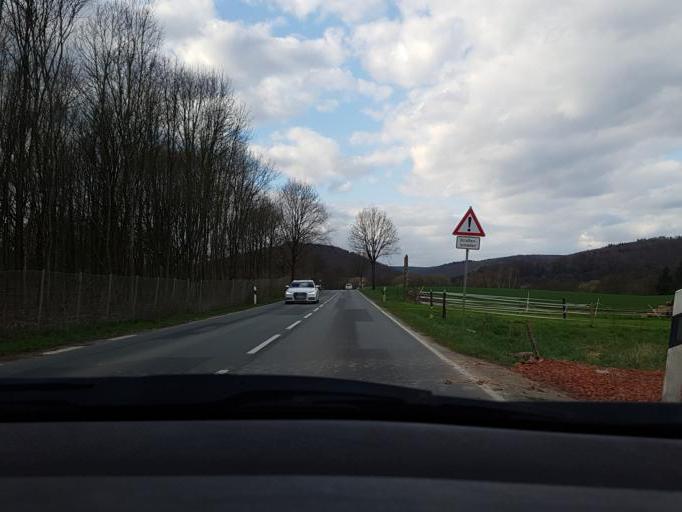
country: DE
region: Lower Saxony
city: Bodenfelde
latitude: 51.6451
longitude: 9.5508
